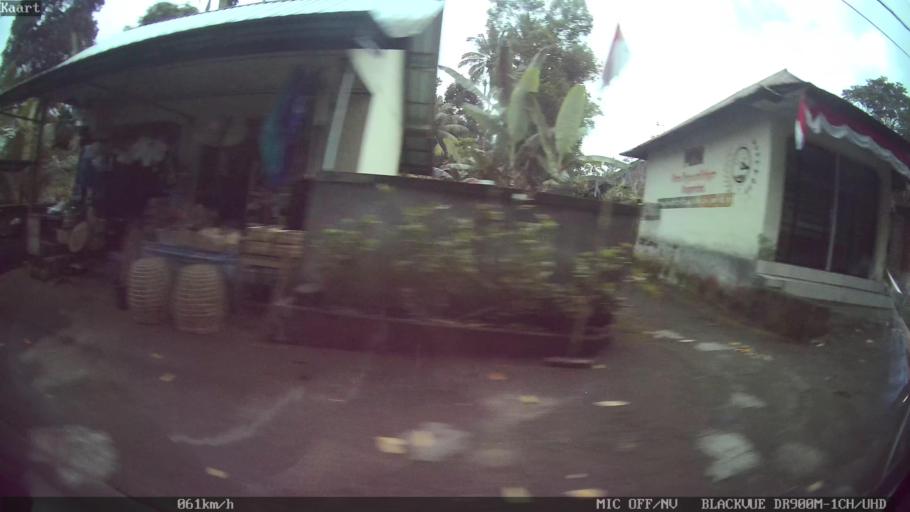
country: ID
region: Bali
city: Banjar Geriana Kangin
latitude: -8.4051
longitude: 115.4398
